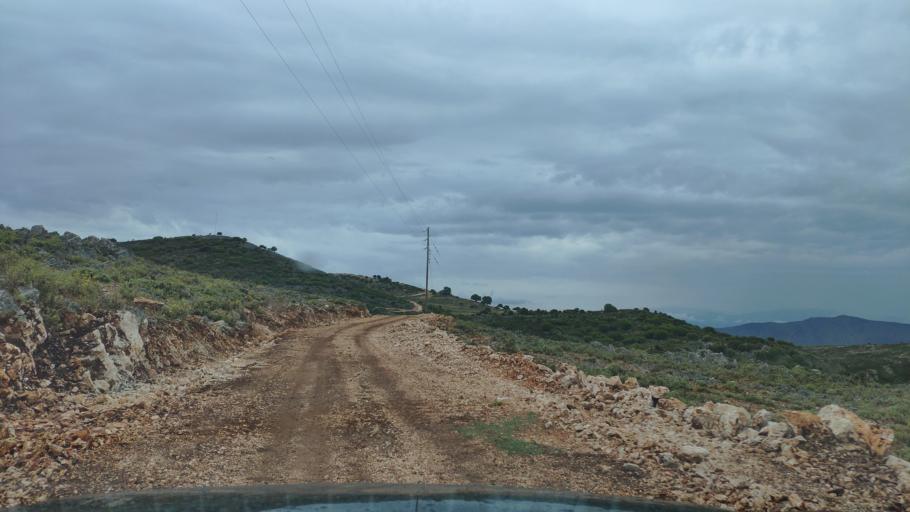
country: GR
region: West Greece
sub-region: Nomos Aitolias kai Akarnanias
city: Archontochorion
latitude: 38.6856
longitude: 21.0301
